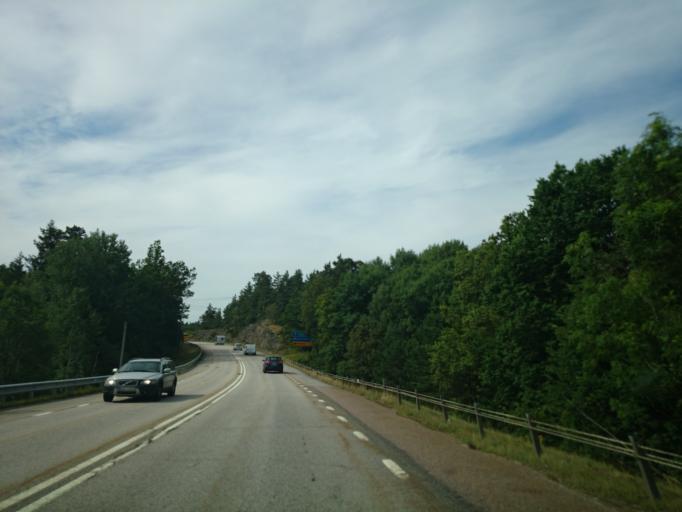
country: SE
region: Kalmar
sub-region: Oskarshamns Kommun
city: Oskarshamn
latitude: 57.4410
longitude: 16.4933
